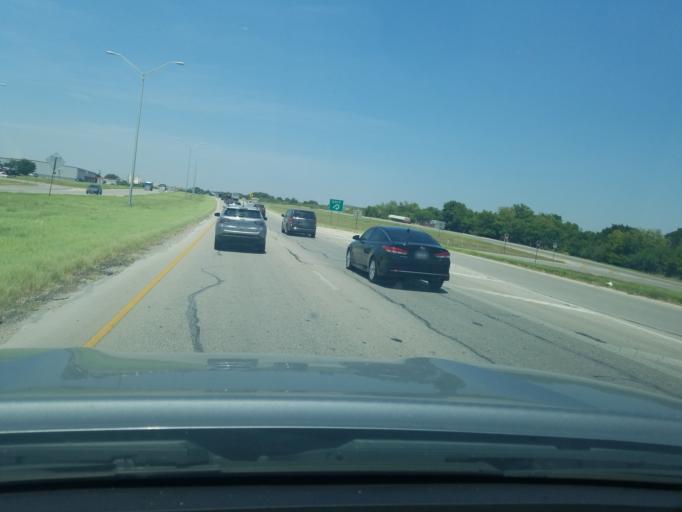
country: US
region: Texas
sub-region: Bexar County
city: Universal City
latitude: 29.5354
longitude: -98.3019
